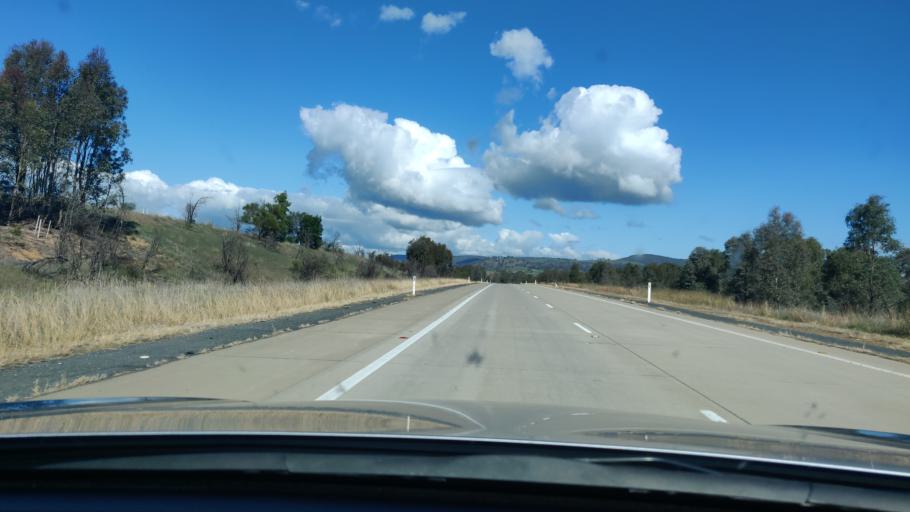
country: AU
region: New South Wales
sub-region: Greater Hume Shire
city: Holbrook
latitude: -35.6475
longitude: 147.4453
